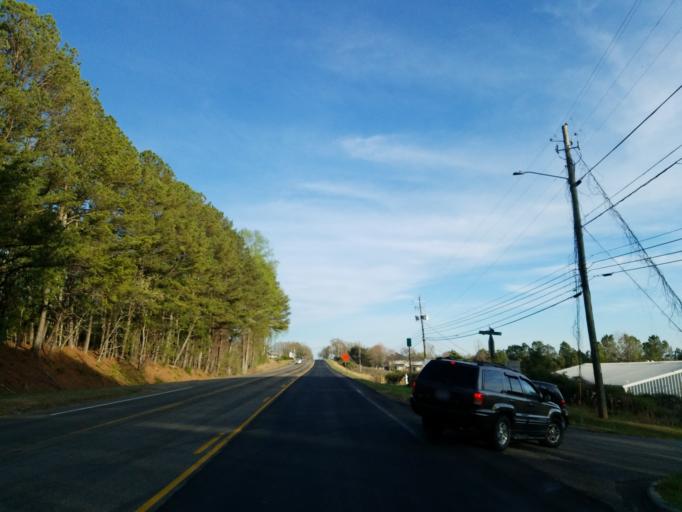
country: US
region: Georgia
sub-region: Pickens County
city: Jasper
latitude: 34.4575
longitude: -84.4109
